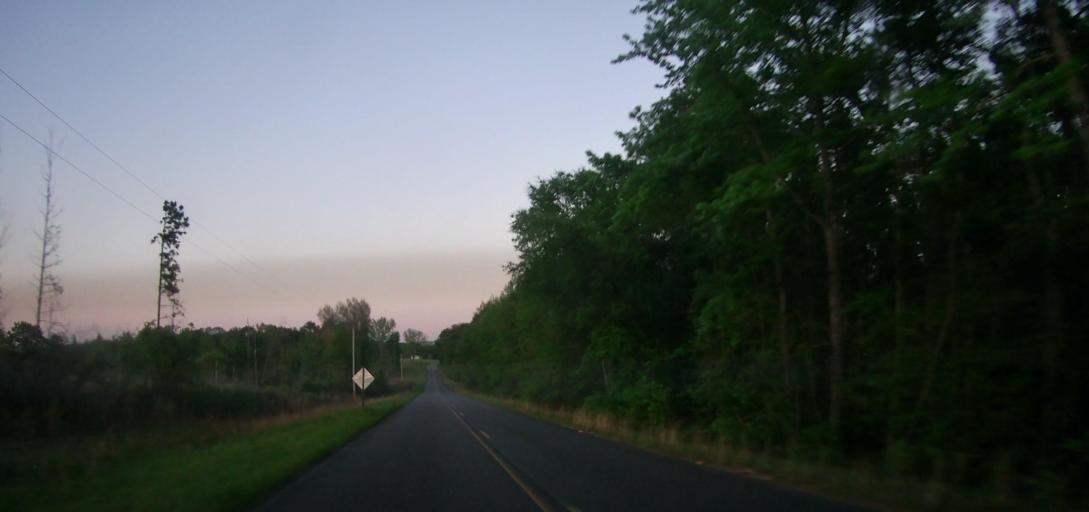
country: US
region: Georgia
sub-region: Marion County
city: Buena Vista
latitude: 32.2556
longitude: -84.6049
